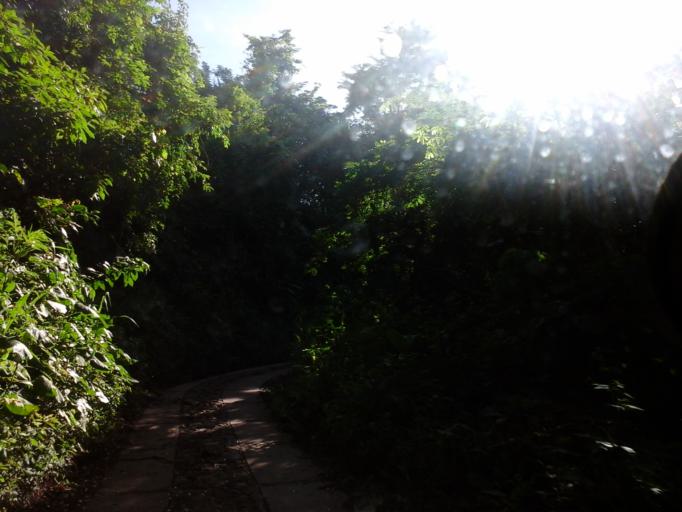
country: CO
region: Cesar
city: San Diego
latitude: 10.2644
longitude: -73.1044
